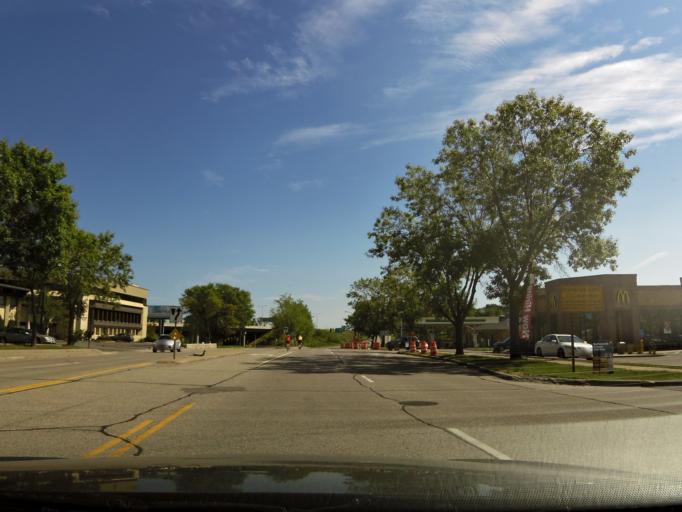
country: US
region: Minnesota
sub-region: Hennepin County
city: Wayzata
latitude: 44.9711
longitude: -93.4957
